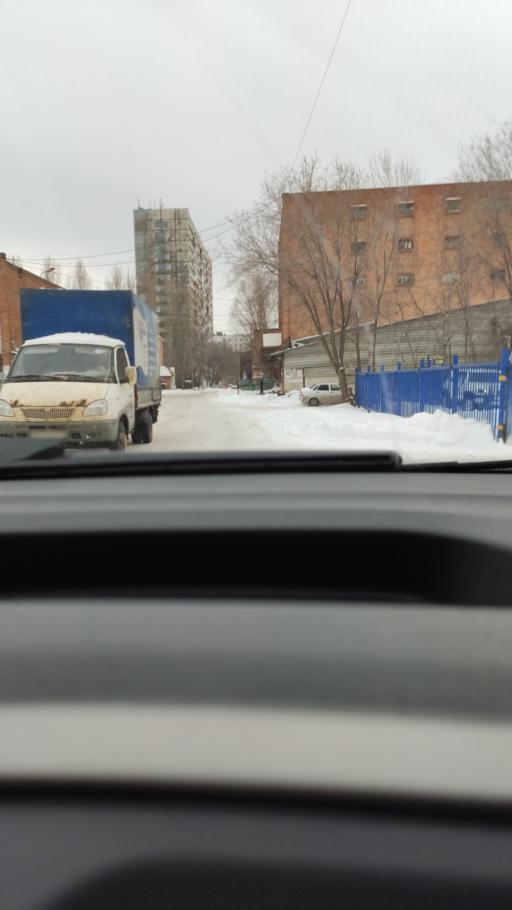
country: RU
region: Samara
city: Tol'yatti
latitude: 53.5402
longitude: 49.2710
